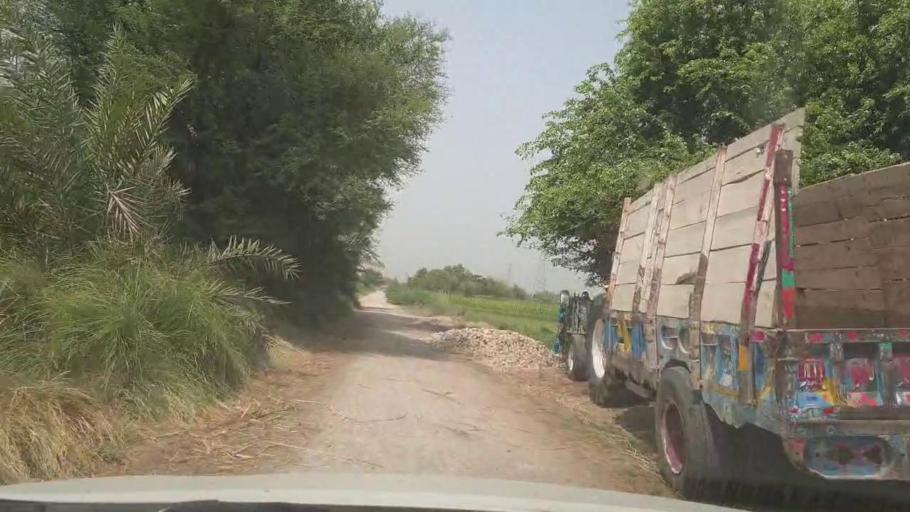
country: PK
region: Sindh
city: Kot Diji
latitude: 27.3515
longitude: 68.7181
